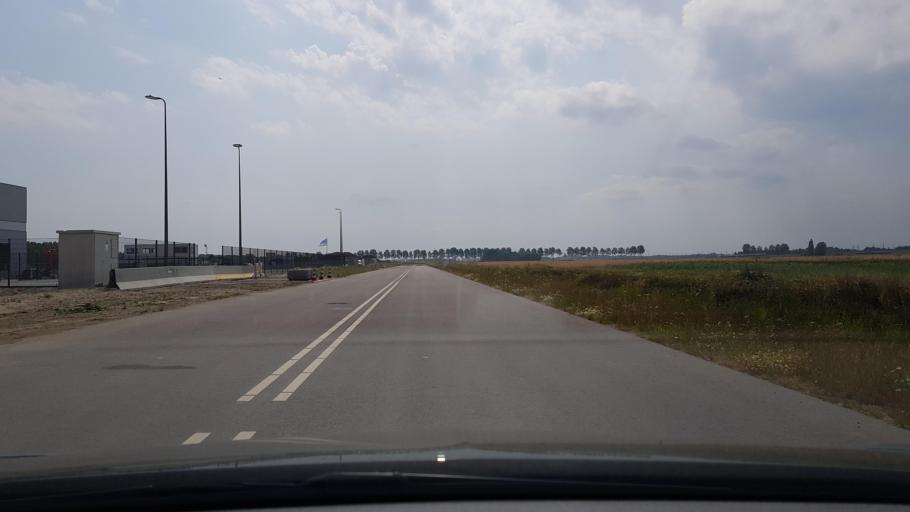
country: NL
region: North Holland
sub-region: Gemeente Haarlemmermeer
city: Hoofddorp
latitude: 52.2828
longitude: 4.6927
